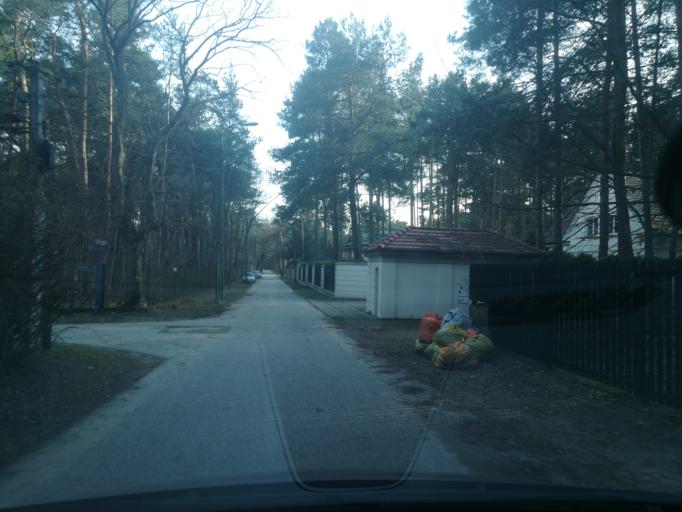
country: PL
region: Masovian Voivodeship
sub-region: Powiat piaseczynski
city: Konstancin-Jeziorna
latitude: 52.0730
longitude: 21.0948
